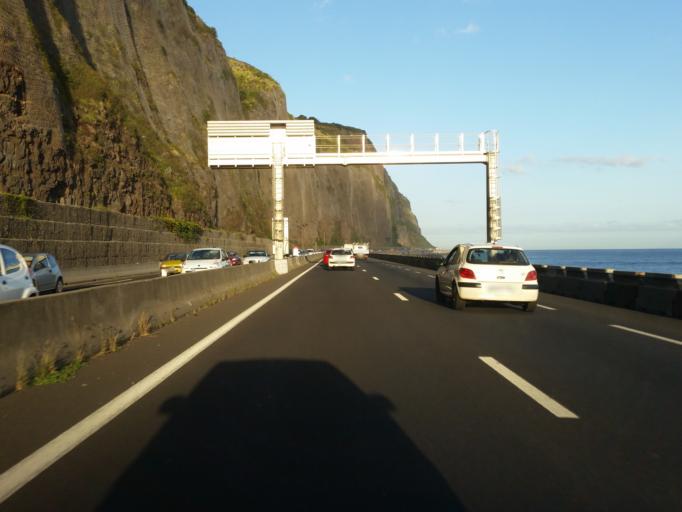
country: RE
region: Reunion
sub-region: Reunion
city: Saint-Denis
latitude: -20.8769
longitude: 55.4141
